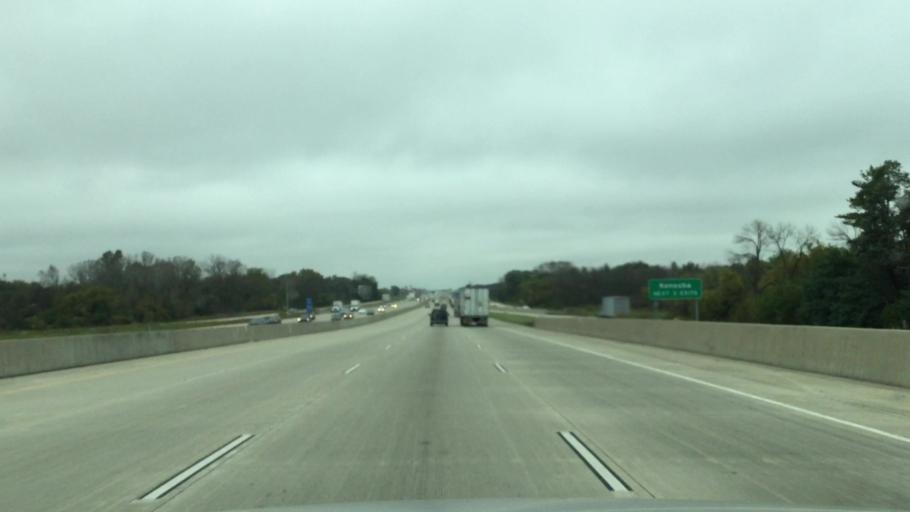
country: US
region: Wisconsin
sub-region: Kenosha County
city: Pleasant Prairie
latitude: 42.5457
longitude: -87.9522
